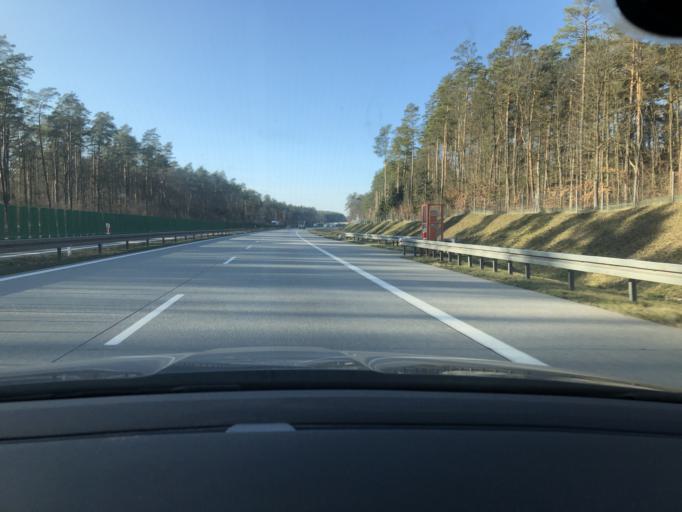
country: PL
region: Lubusz
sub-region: Powiat swiebodzinski
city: Lagow
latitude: 52.3121
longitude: 15.2141
